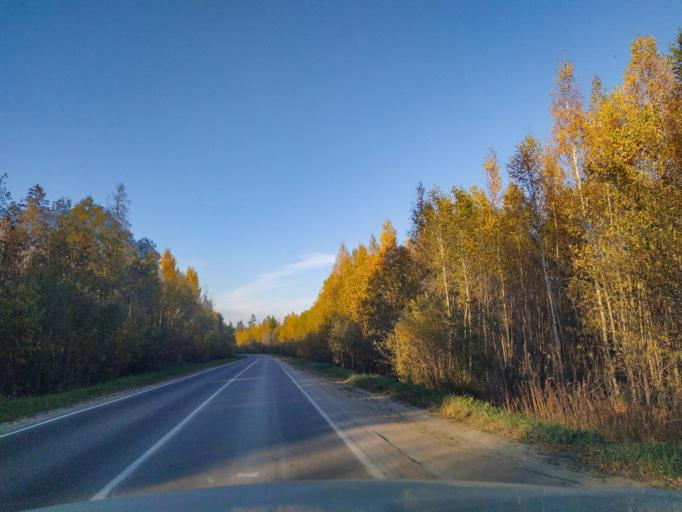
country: RU
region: Leningrad
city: Siverskiy
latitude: 59.3000
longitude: 30.0352
